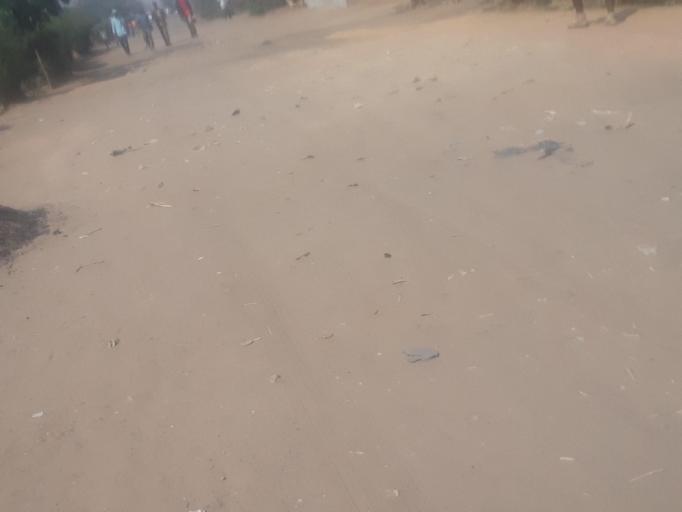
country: ZM
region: Lusaka
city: Lusaka
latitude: -15.3543
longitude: 28.2885
